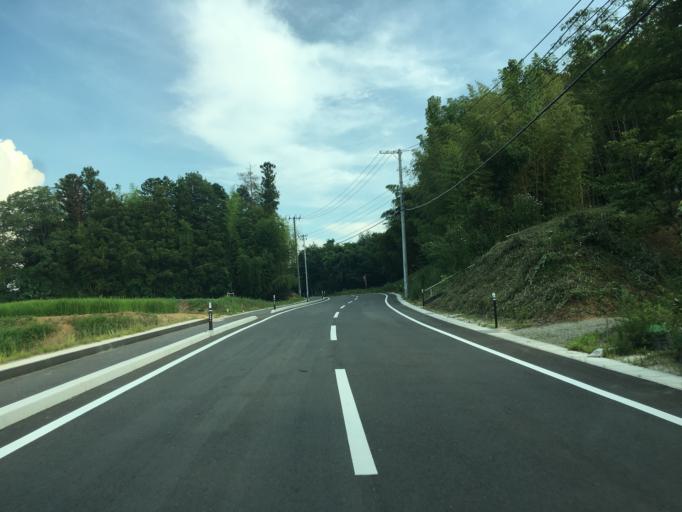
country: JP
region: Fukushima
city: Nihommatsu
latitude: 37.5594
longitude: 140.4276
